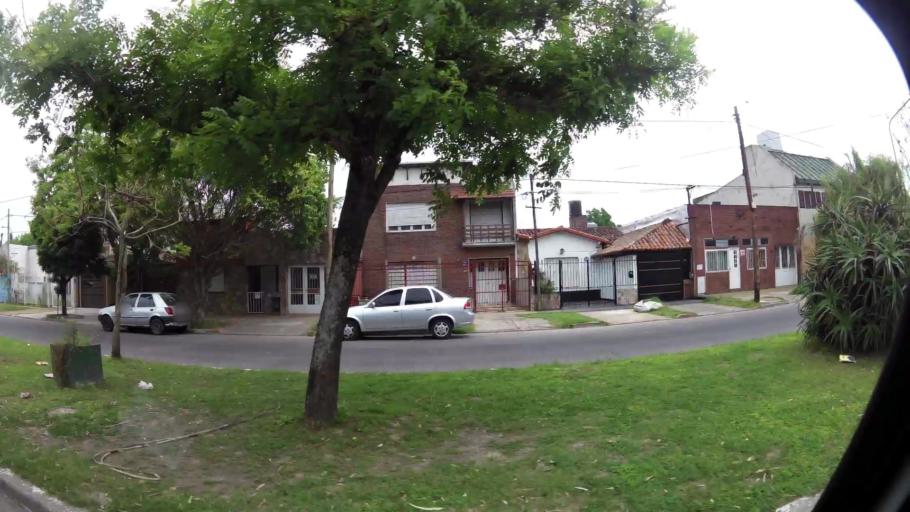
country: AR
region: Buenos Aires
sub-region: Partido de La Plata
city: La Plata
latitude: -34.8960
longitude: -57.9763
